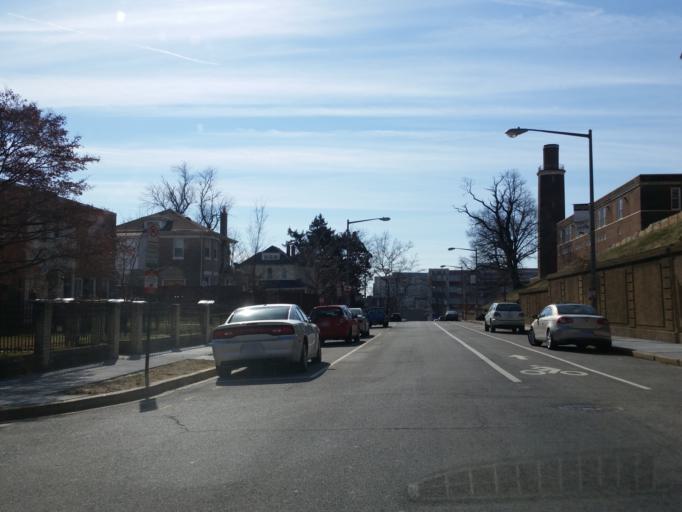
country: US
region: Washington, D.C.
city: Washington, D.C.
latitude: 38.9149
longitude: -77.0035
